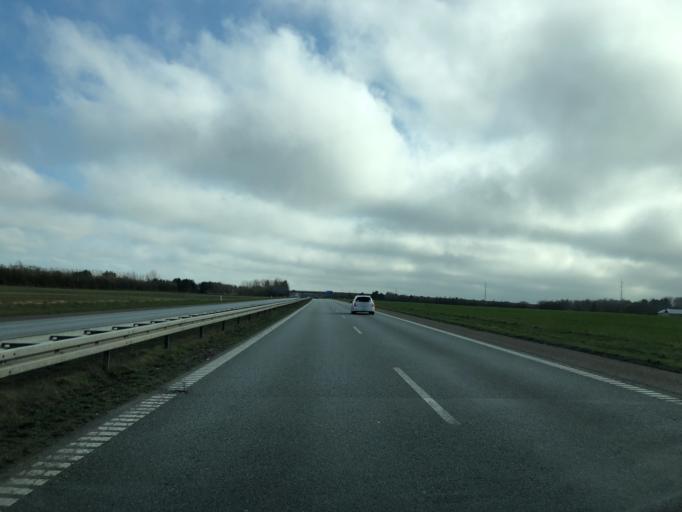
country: DK
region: North Denmark
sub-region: Hjorring Kommune
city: Hjorring
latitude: 57.4362
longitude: 10.0355
